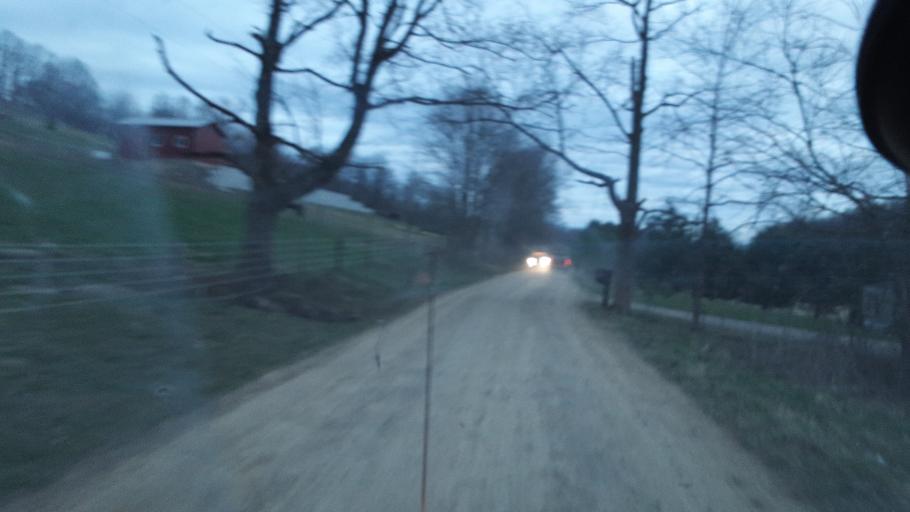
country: US
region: Ohio
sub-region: Coshocton County
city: West Lafayette
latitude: 40.3555
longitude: -81.7726
